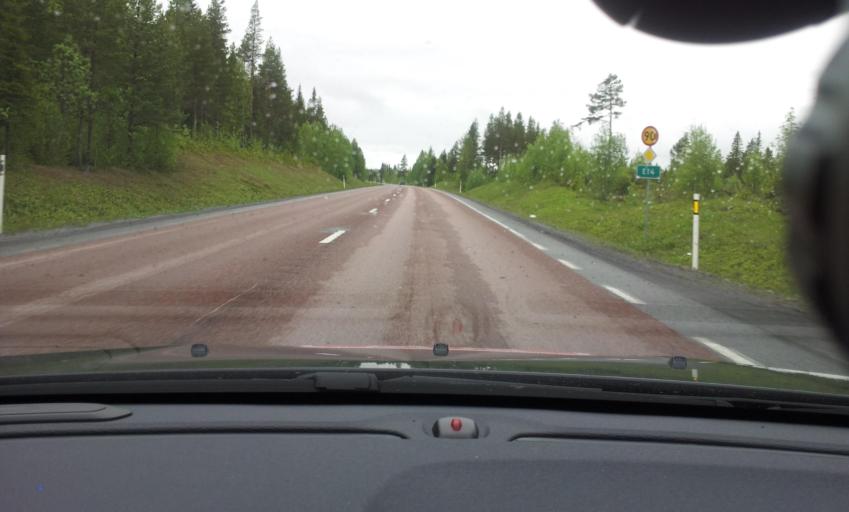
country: SE
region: Jaemtland
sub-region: Krokoms Kommun
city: Valla
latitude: 63.3239
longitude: 13.9489
